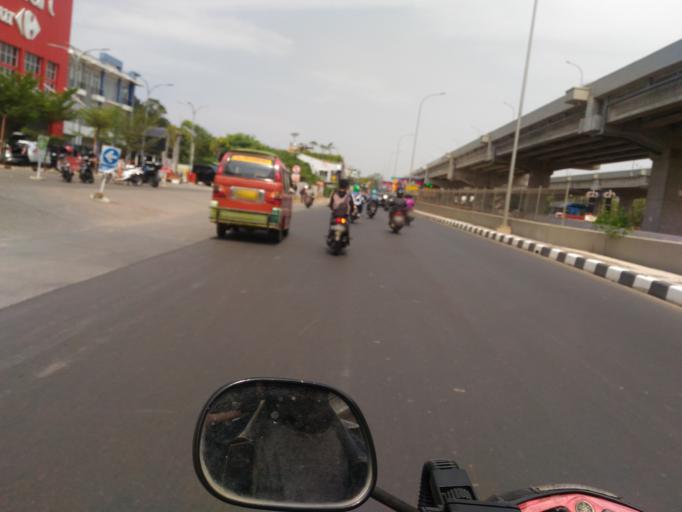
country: ID
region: West Java
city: Bekasi
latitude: -6.2484
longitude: 106.9314
